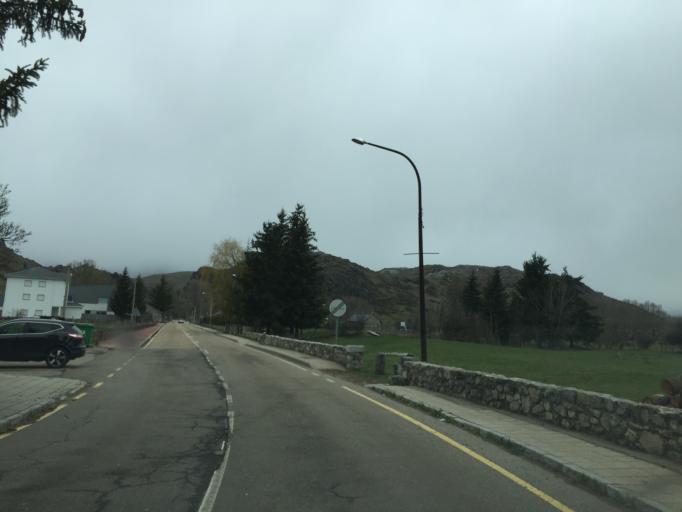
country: ES
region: Castille and Leon
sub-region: Provincia de Leon
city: San Emiliano
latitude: 42.9707
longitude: -6.0013
